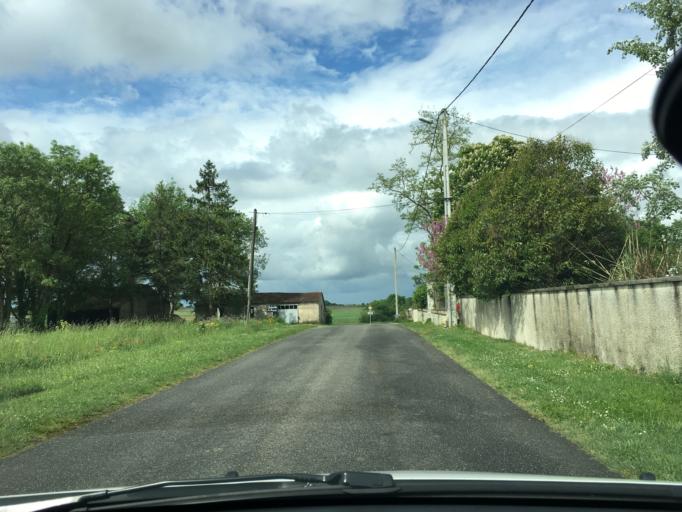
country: FR
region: Aquitaine
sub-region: Departement de la Gironde
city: Vertheuil
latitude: 45.3220
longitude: -0.8322
